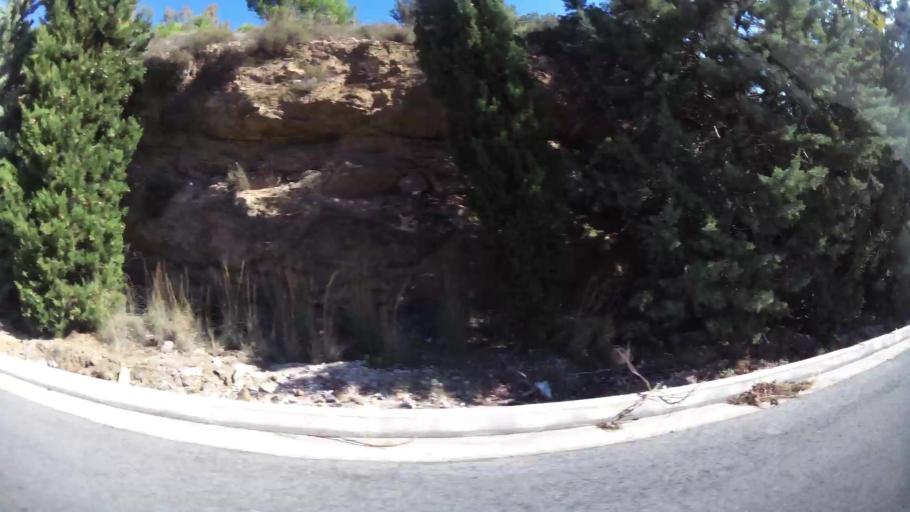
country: GR
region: Attica
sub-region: Nomarchia Anatolikis Attikis
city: Dhrafi
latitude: 38.0414
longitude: 23.8988
